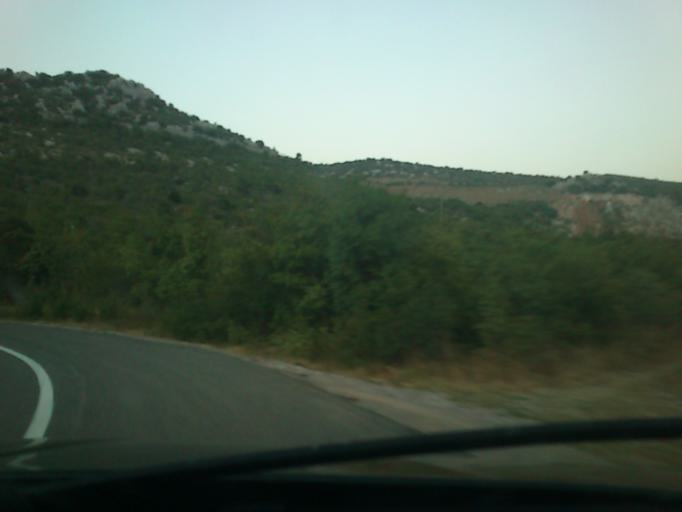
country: HR
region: Licko-Senjska
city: Senj
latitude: 44.9183
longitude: 14.9185
